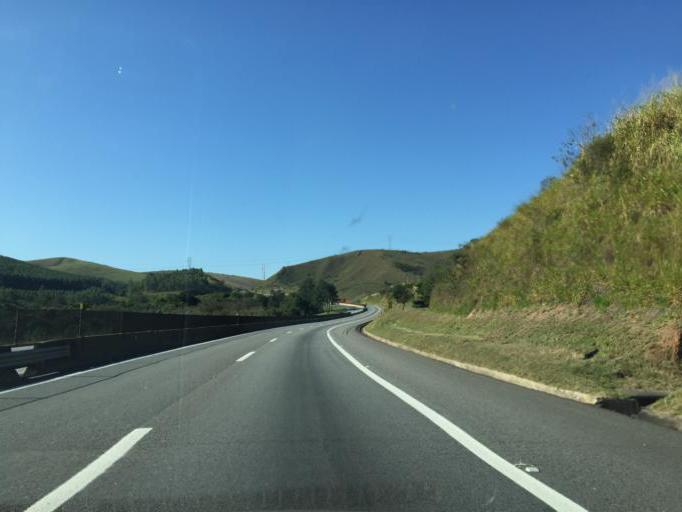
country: BR
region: Sao Paulo
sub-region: Cruzeiro
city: Cruzeiro
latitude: -22.6485
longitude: -44.9555
